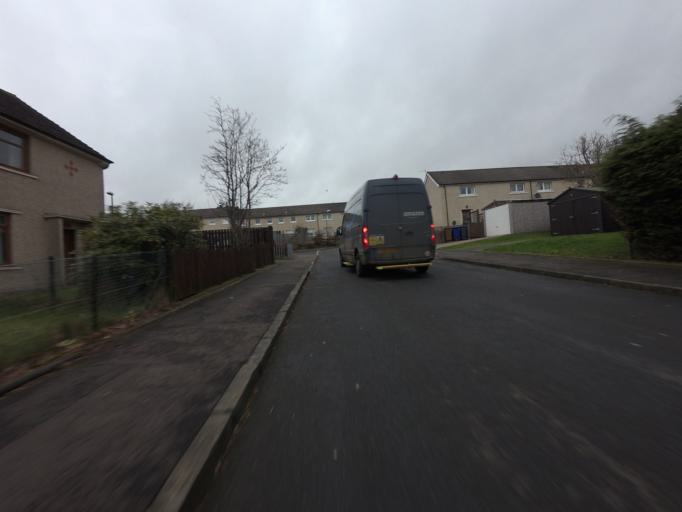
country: GB
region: Scotland
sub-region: West Lothian
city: Livingston
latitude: 55.9018
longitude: -3.5659
